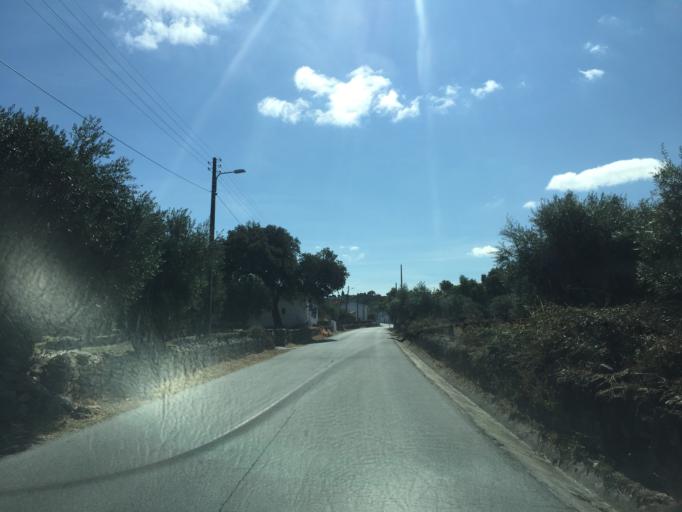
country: PT
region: Portalegre
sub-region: Marvao
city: Marvao
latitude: 39.4259
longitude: -7.3543
